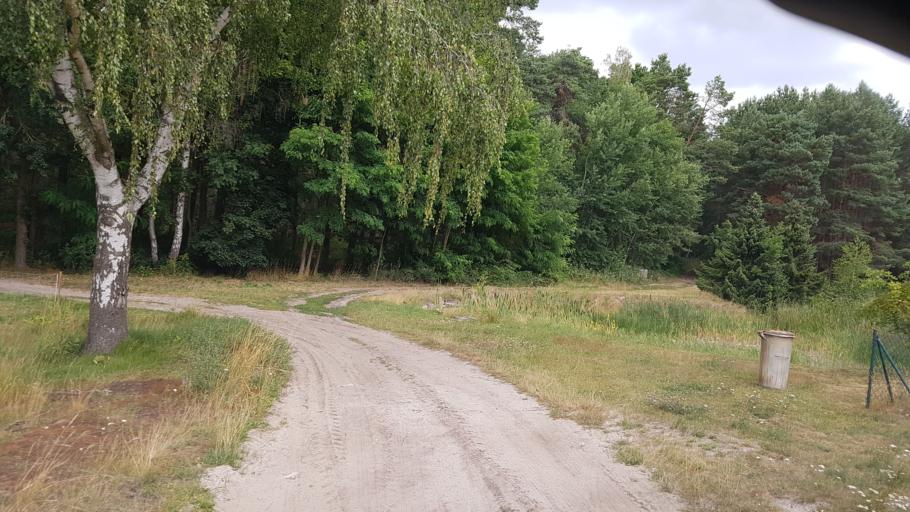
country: DE
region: Brandenburg
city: Crinitz
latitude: 51.7082
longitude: 13.7264
